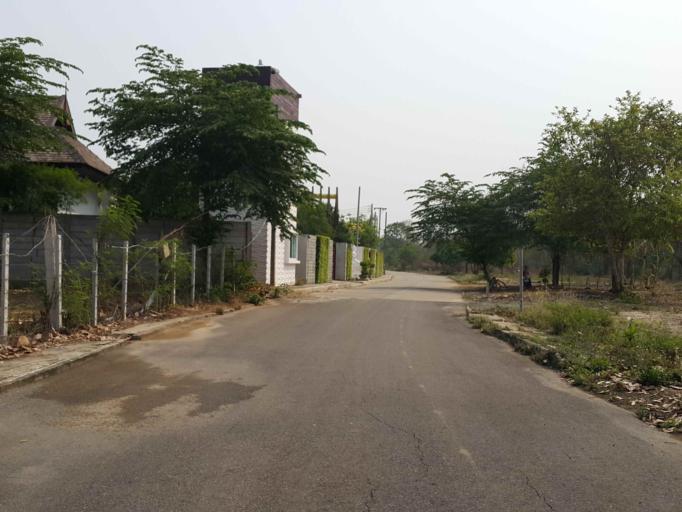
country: TH
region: Chiang Mai
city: Saraphi
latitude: 18.7580
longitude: 99.0578
